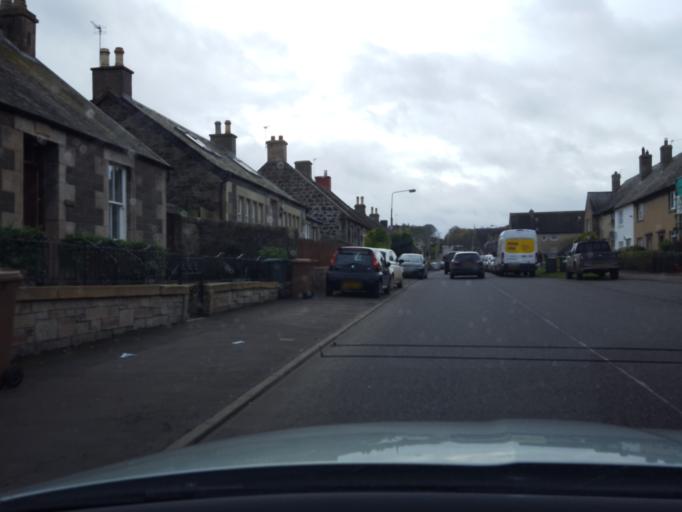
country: GB
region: Scotland
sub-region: Edinburgh
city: Ratho
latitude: 55.9212
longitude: -3.3825
